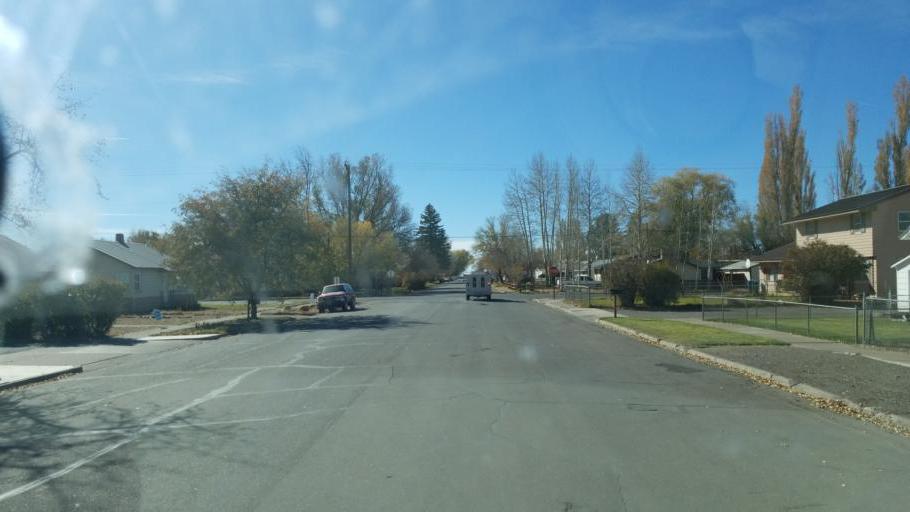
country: US
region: Colorado
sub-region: Rio Grande County
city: Monte Vista
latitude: 37.5751
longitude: -106.1468
